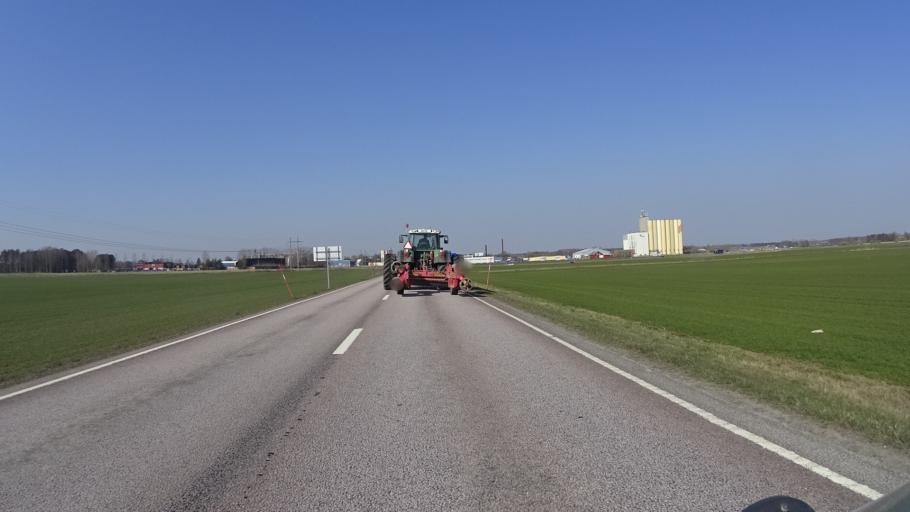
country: SE
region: OEstergoetland
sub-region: Mjolby Kommun
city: Mjolby
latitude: 58.3922
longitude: 15.1117
